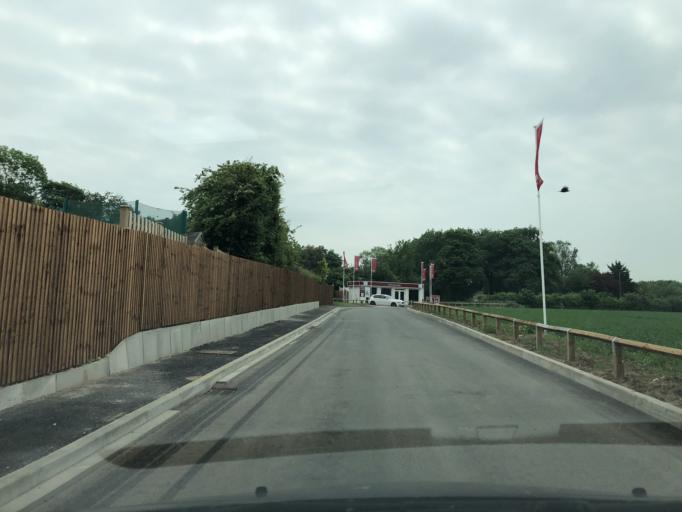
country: GB
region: England
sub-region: North Yorkshire
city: Boroughbridge
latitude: 54.0936
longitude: -1.4024
